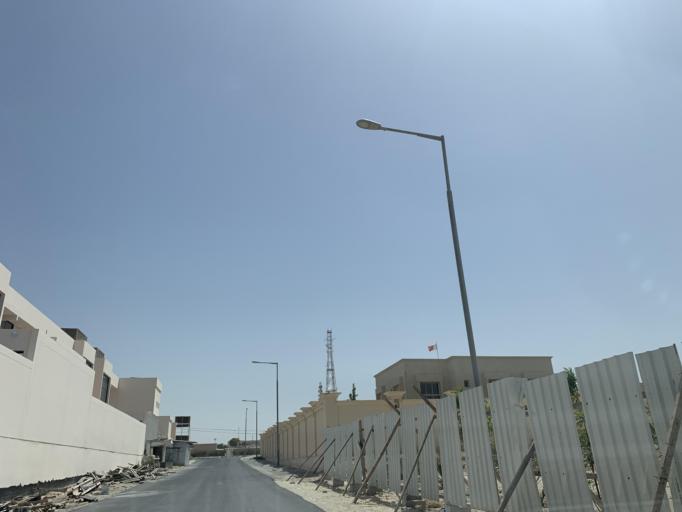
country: BH
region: Northern
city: Ar Rifa'
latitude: 26.1478
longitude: 50.5459
